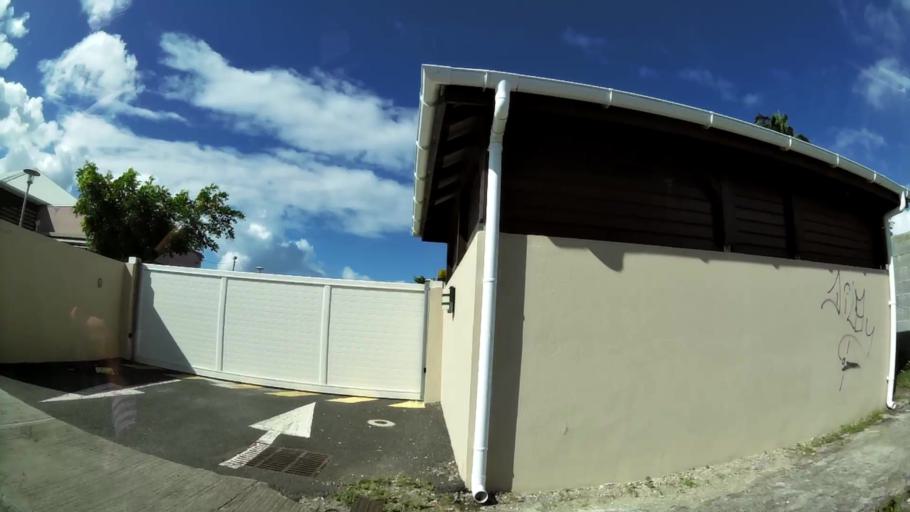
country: GP
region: Guadeloupe
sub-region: Guadeloupe
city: Port-Louis
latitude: 16.4149
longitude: -61.5295
